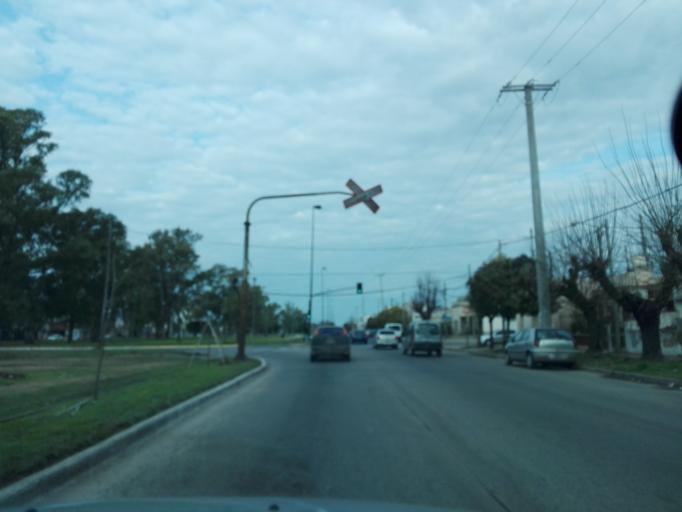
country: AR
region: Buenos Aires
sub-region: Partido de La Plata
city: La Plata
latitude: -34.9444
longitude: -57.9660
